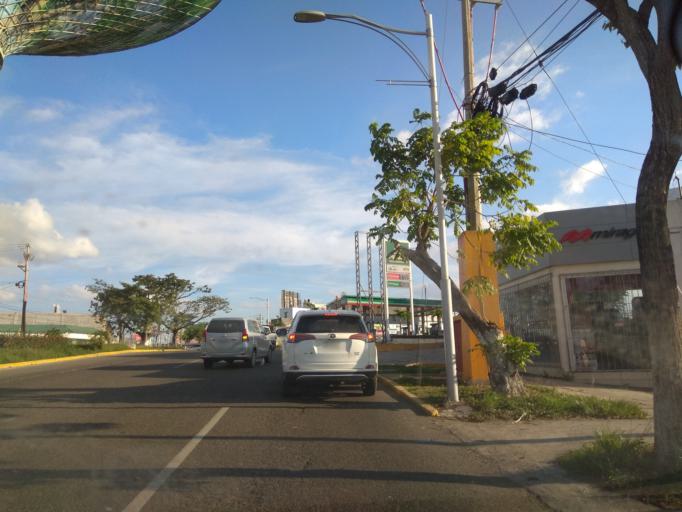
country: MX
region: Tabasco
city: Villahermosa
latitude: 17.9938
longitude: -92.9471
